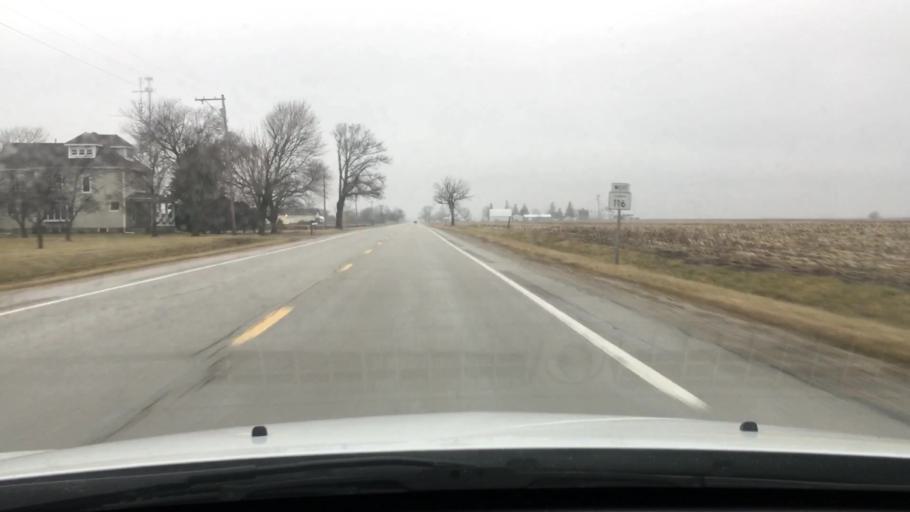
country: US
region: Illinois
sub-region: Livingston County
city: Flanagan
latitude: 40.8709
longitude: -88.8732
